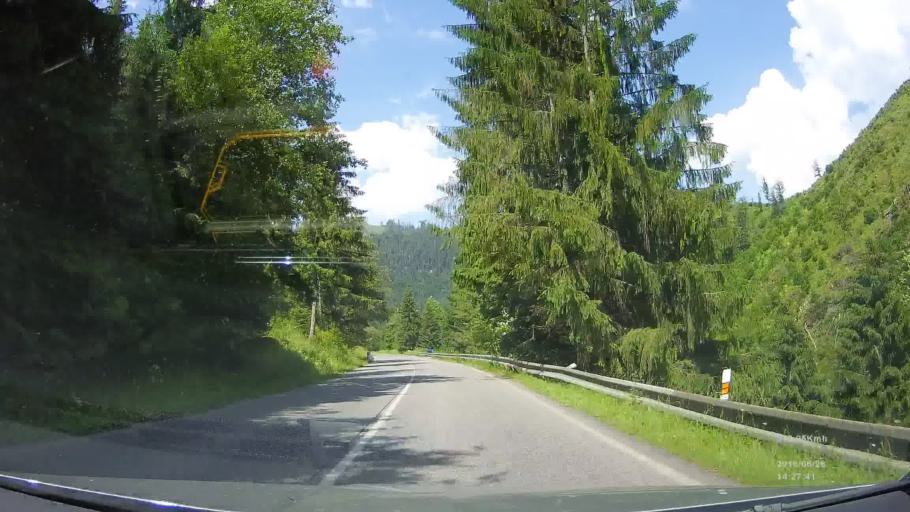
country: SK
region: Zilinsky
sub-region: Okres Zilina
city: Liptovsky Hradok
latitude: 48.9693
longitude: 19.7762
